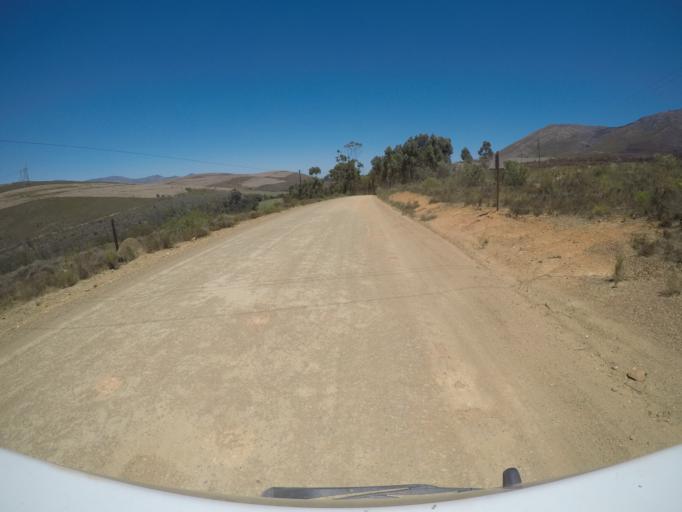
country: ZA
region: Western Cape
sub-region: Overberg District Municipality
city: Caledon
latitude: -34.1973
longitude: 19.2219
